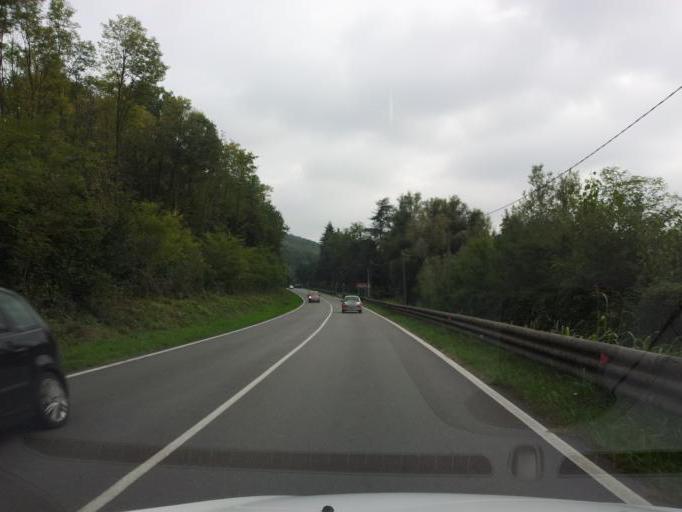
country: IT
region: Lombardy
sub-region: Provincia di Varese
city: Varano Borghi
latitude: 45.7605
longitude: 8.7004
